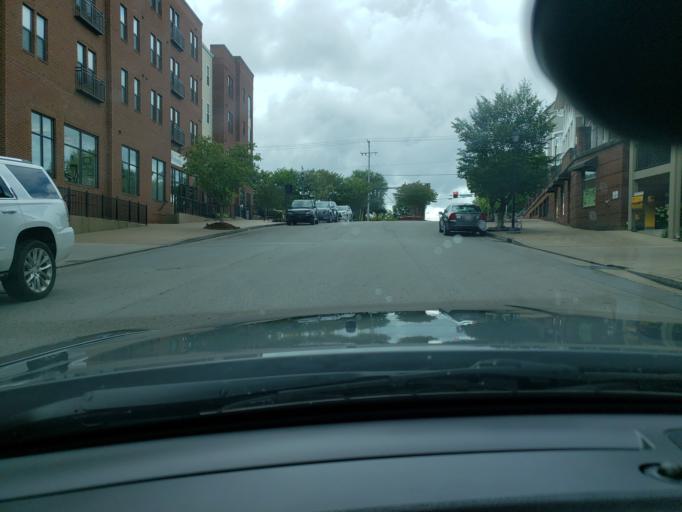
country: US
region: Tennessee
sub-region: Williamson County
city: Brentwood Estates
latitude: 36.0255
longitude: -86.7119
